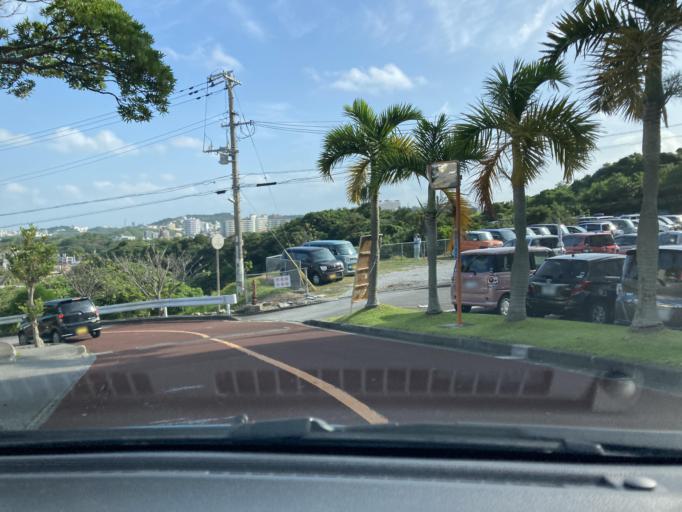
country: JP
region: Okinawa
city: Ginowan
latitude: 26.2287
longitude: 127.7412
